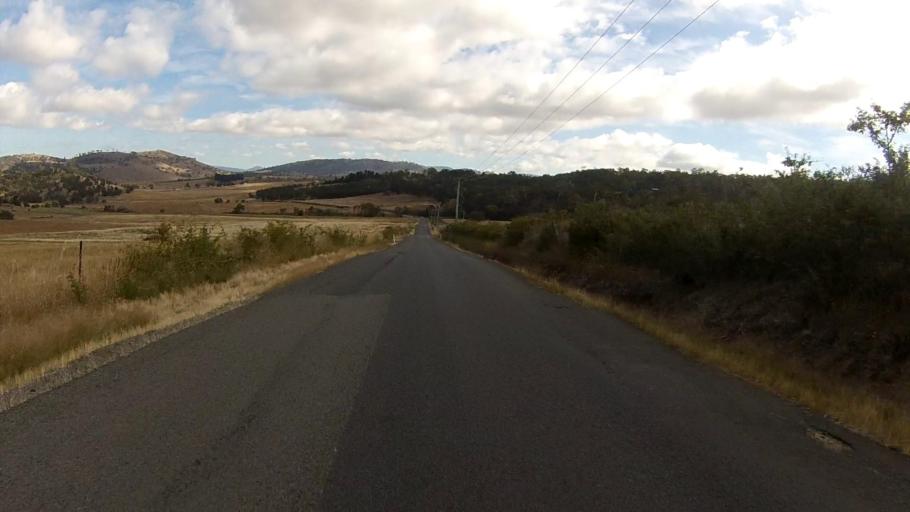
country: AU
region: Tasmania
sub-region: Brighton
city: Old Beach
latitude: -42.7573
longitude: 147.3047
